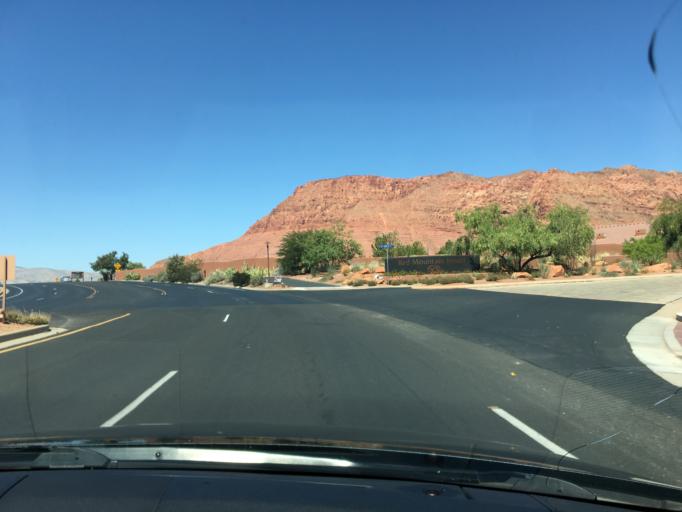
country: US
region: Utah
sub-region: Washington County
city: Ivins
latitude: 37.1684
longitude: -113.6502
